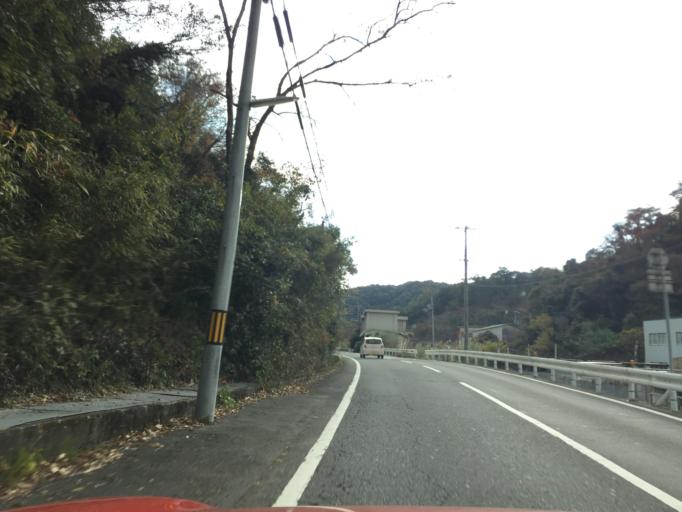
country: JP
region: Wakayama
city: Kainan
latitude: 34.1656
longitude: 135.2519
